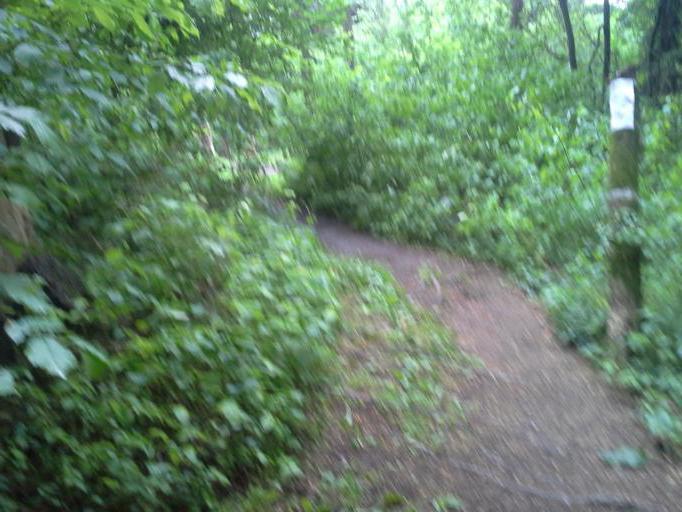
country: RU
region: Moskovskaya
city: Moskovskiy
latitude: 55.5864
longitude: 37.3391
